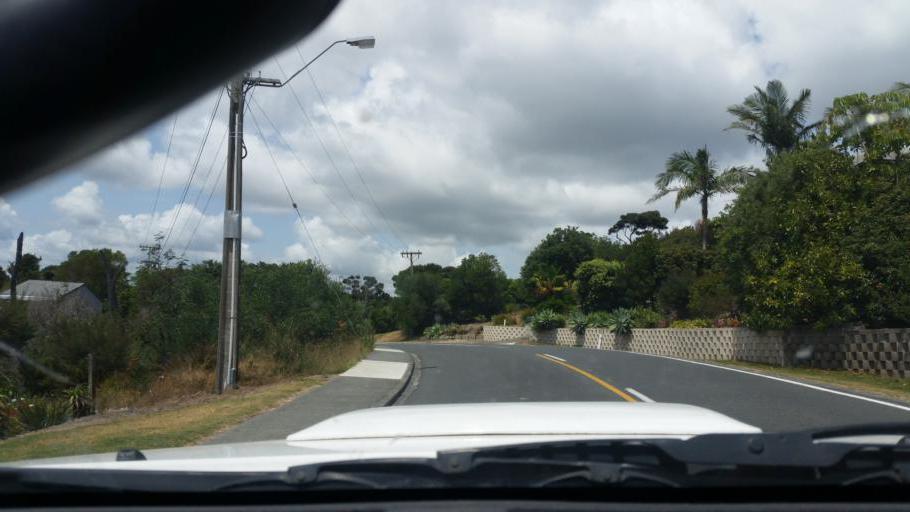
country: NZ
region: Auckland
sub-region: Auckland
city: Wellsford
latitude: -36.0928
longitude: 174.5846
